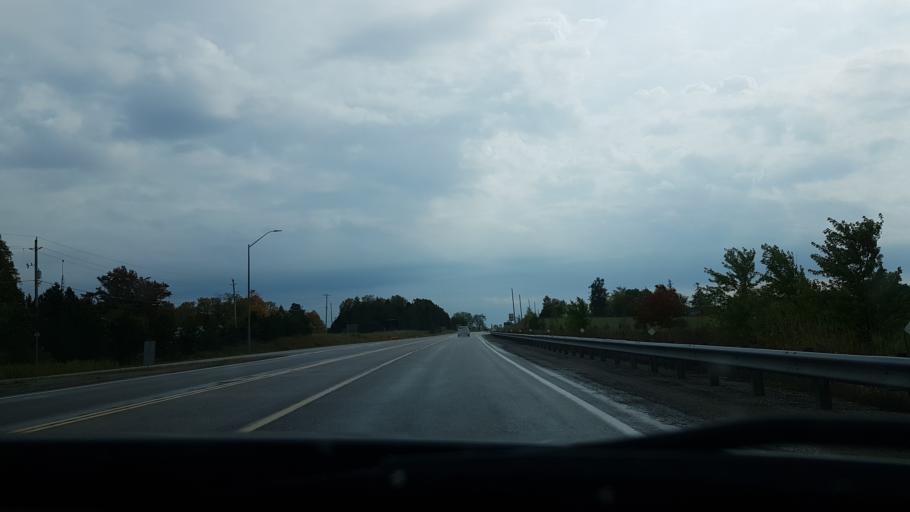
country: CA
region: Ontario
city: Omemee
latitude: 44.4853
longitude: -78.7607
